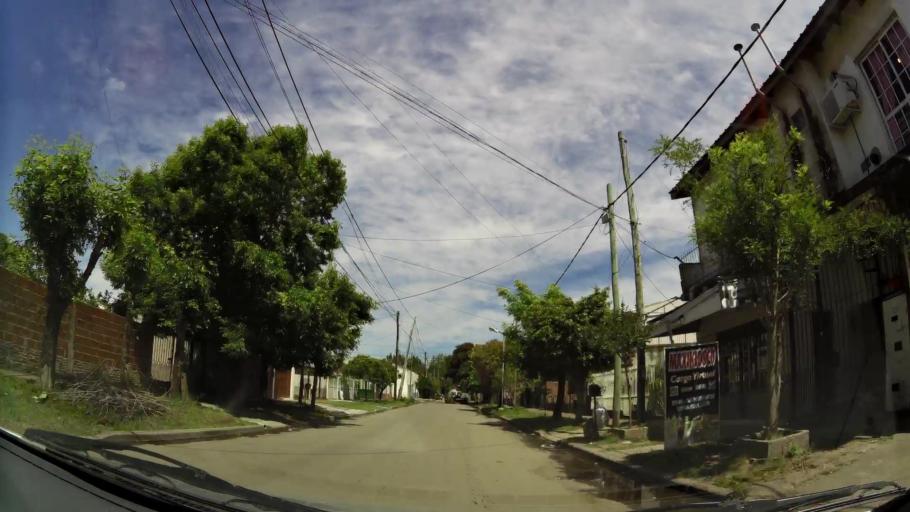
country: AR
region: Buenos Aires
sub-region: Partido de Quilmes
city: Quilmes
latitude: -34.7475
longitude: -58.2948
